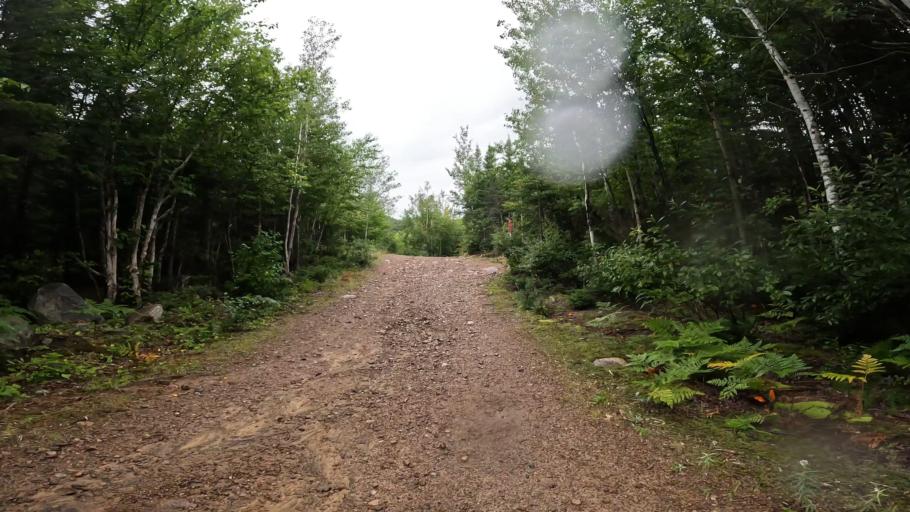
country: CA
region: Quebec
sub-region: Capitale-Nationale
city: La Malbaie
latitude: 47.8052
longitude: -70.4840
